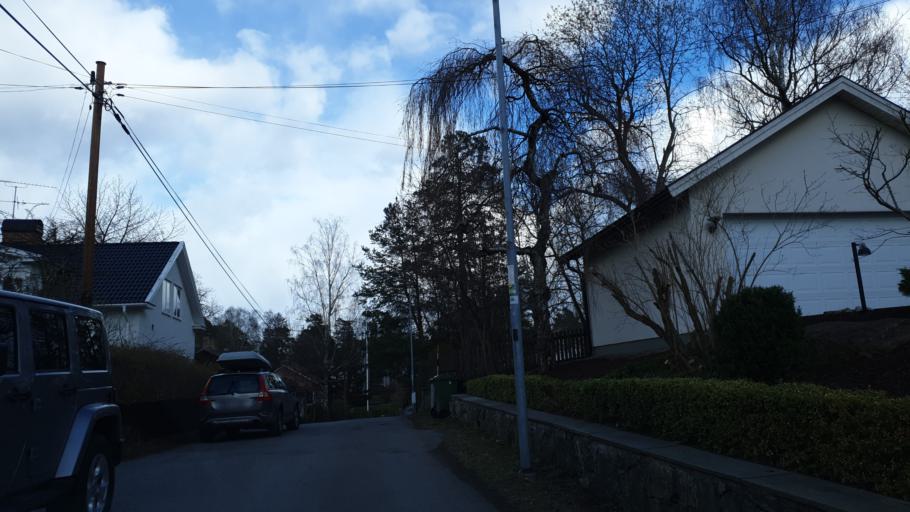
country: SE
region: Stockholm
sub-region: Lidingo
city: Lidingoe
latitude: 59.3728
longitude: 18.1175
